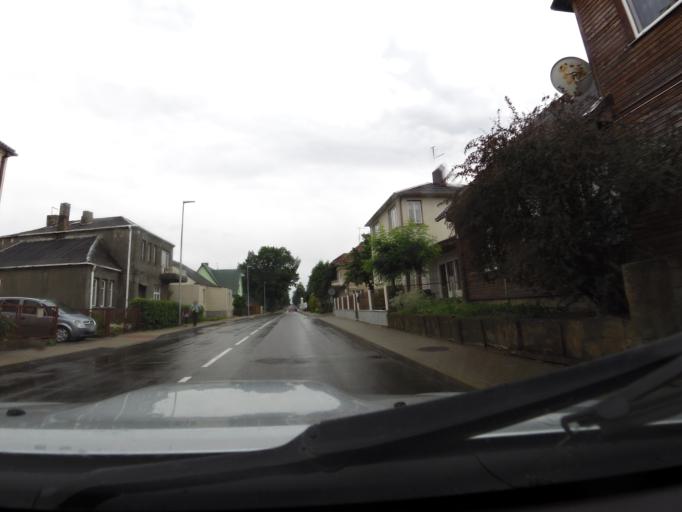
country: LT
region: Marijampoles apskritis
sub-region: Marijampole Municipality
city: Marijampole
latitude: 54.5512
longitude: 23.3456
